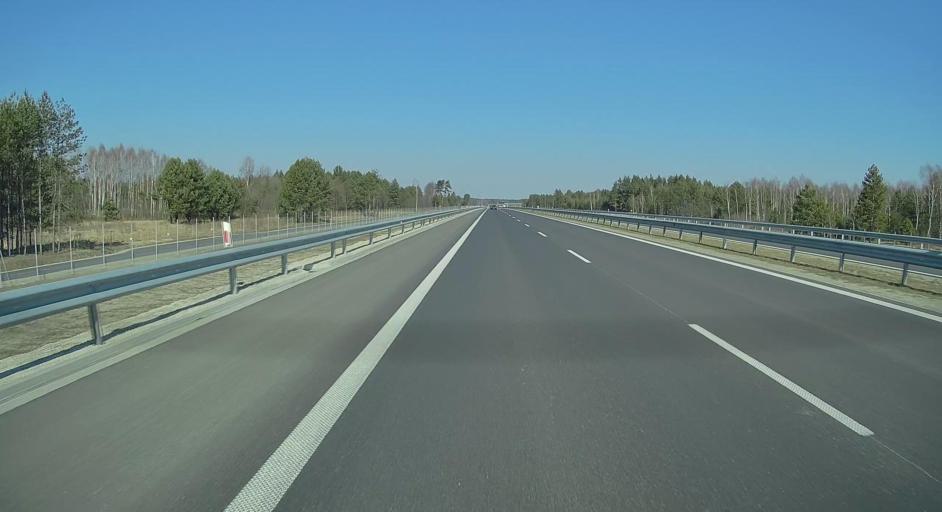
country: PL
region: Subcarpathian Voivodeship
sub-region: Powiat nizanski
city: Konczyce
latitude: 50.4494
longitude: 22.1405
